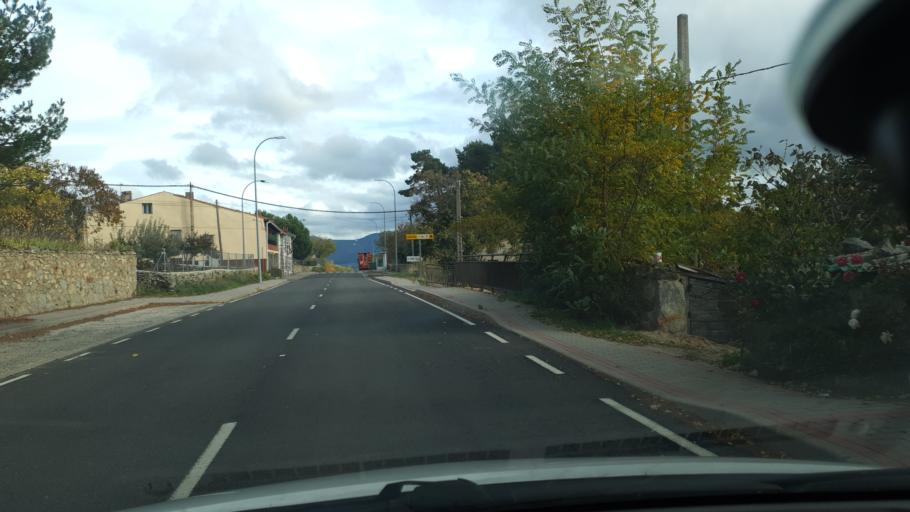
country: ES
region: Castille and Leon
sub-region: Provincia de Avila
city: Hoyocasero
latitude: 40.3982
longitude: -4.9766
